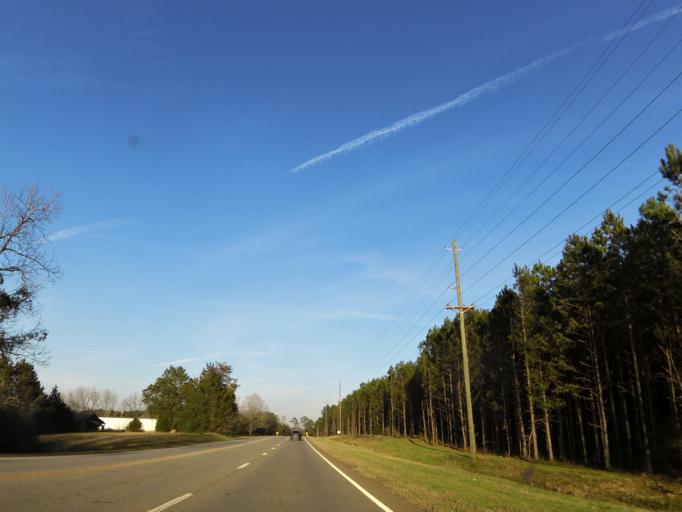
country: US
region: Georgia
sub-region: Sumter County
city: Americus
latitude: 32.0539
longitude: -84.3251
